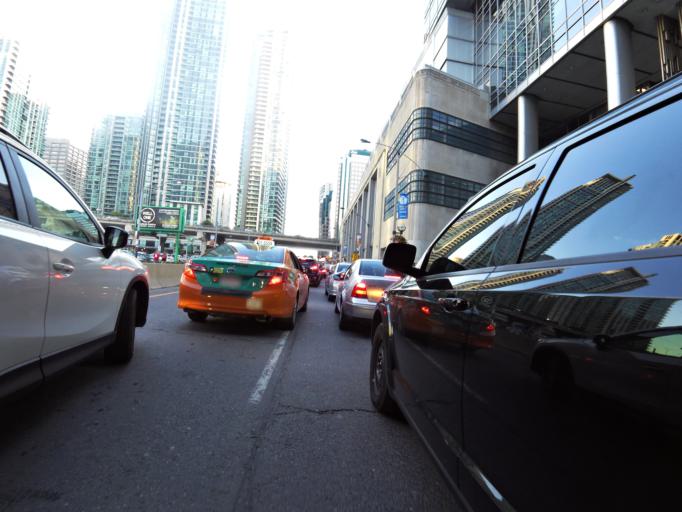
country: CA
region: Ontario
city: Toronto
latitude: 43.6443
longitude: -79.3784
